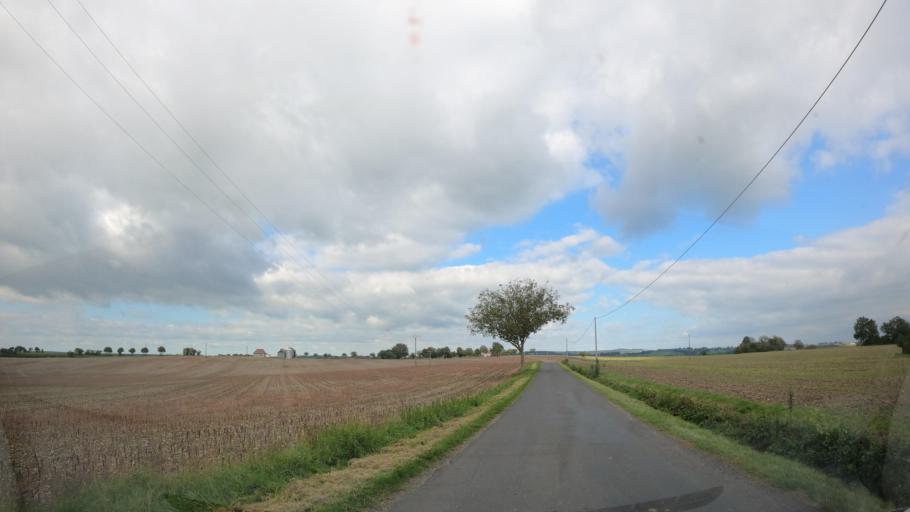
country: FR
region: Auvergne
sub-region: Departement de l'Allier
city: Lapalisse
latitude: 46.3537
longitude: 3.6162
